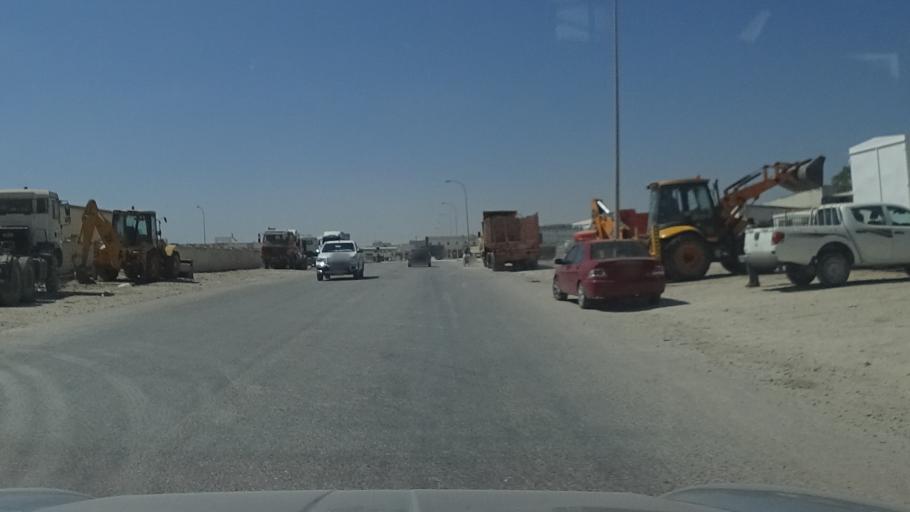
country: OM
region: Zufar
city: Salalah
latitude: 17.0289
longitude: 54.0443
